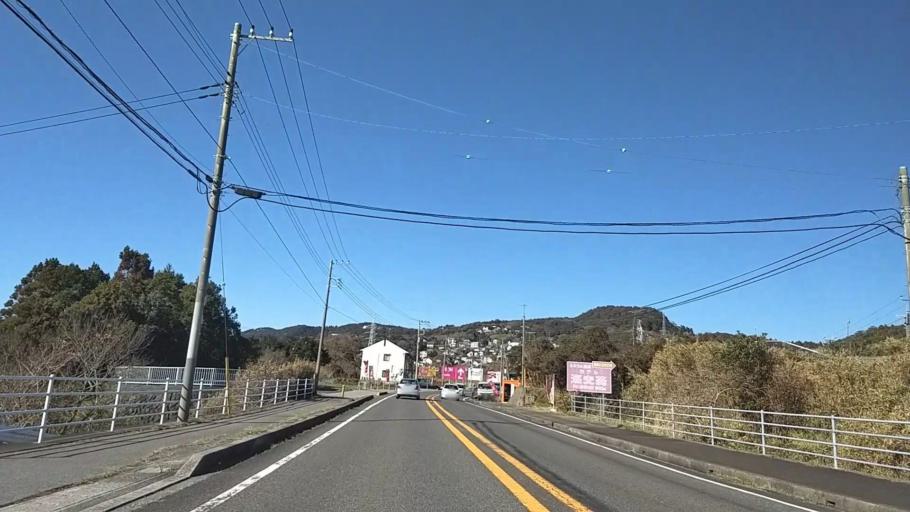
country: JP
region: Chiba
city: Kawaguchi
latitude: 35.0874
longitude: 140.0917
